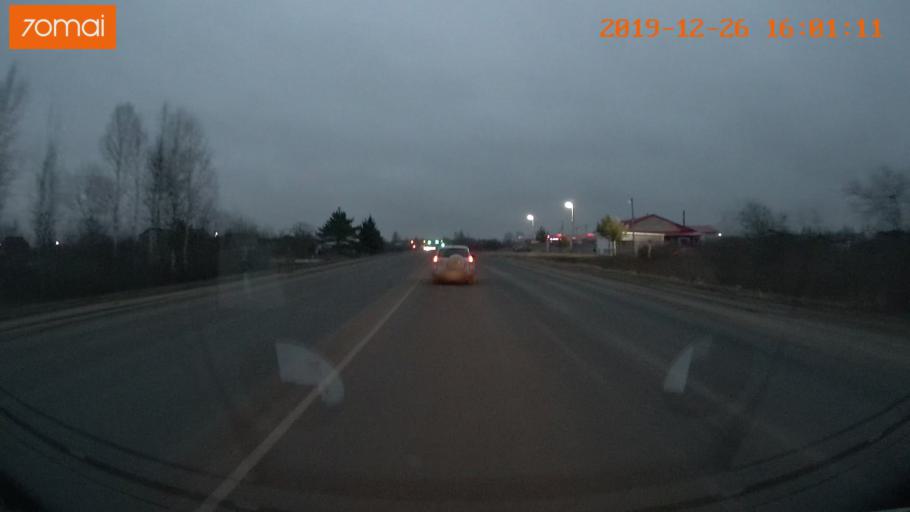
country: RU
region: Jaroslavl
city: Rybinsk
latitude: 58.0171
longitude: 38.8147
